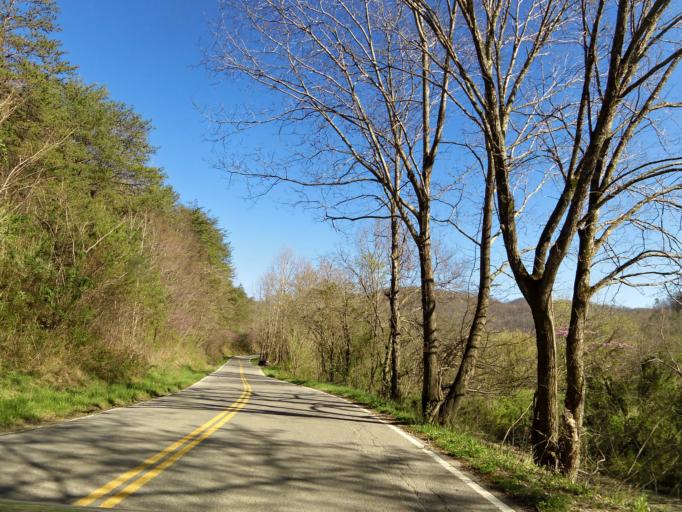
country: US
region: Tennessee
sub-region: Scott County
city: Huntsville
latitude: 36.3319
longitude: -84.3799
